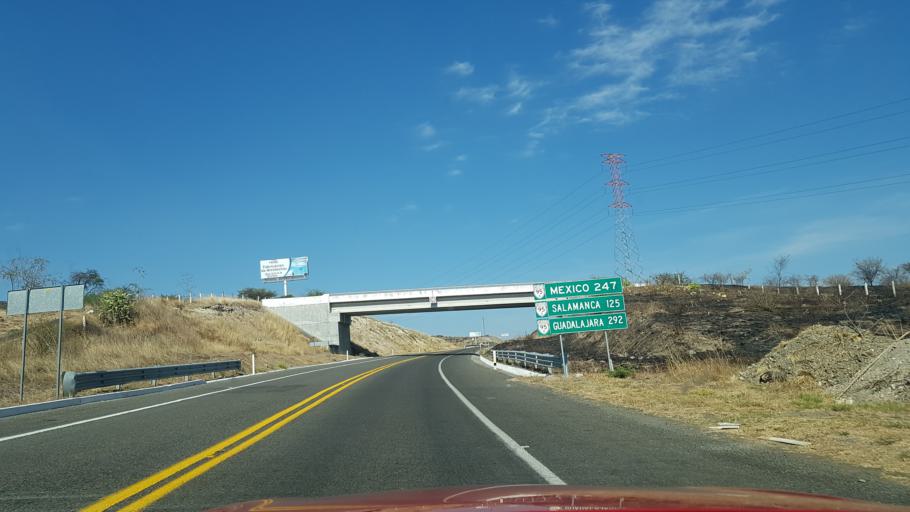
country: MX
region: Michoacan
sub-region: Morelia
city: Fraccionamiento Mision del Valle
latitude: 19.7446
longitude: -101.0972
